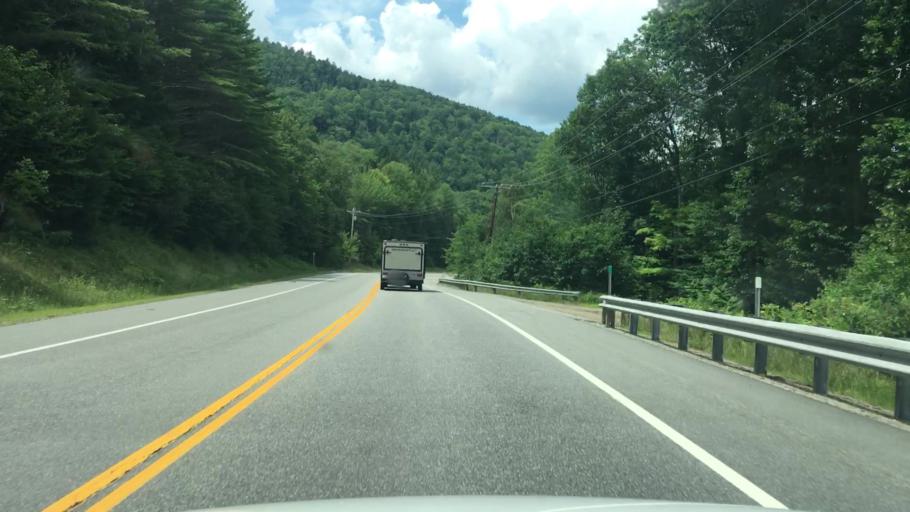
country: US
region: New Hampshire
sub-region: Grafton County
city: Rumney
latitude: 43.8426
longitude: -71.9054
